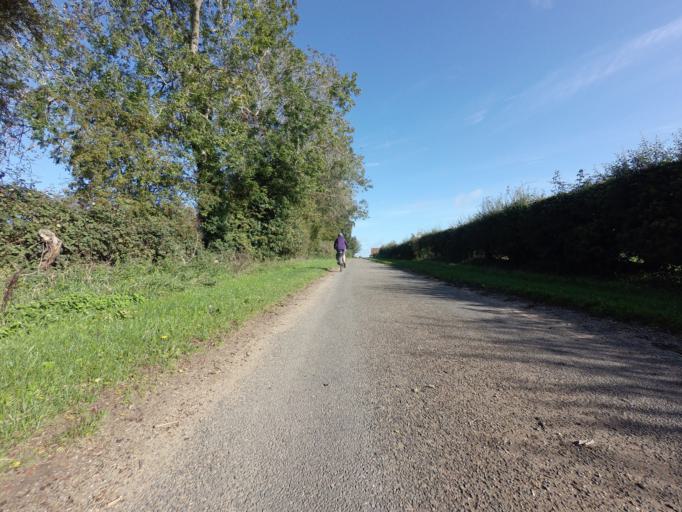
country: GB
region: England
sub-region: Norfolk
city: Dersingham
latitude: 52.8276
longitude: 0.6721
